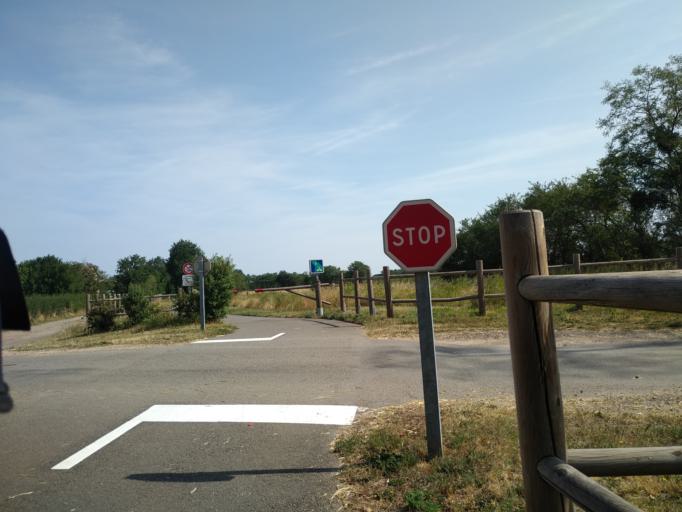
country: FR
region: Bourgogne
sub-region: Departement de Saone-et-Loire
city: Marcigny
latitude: 46.3220
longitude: 4.0285
